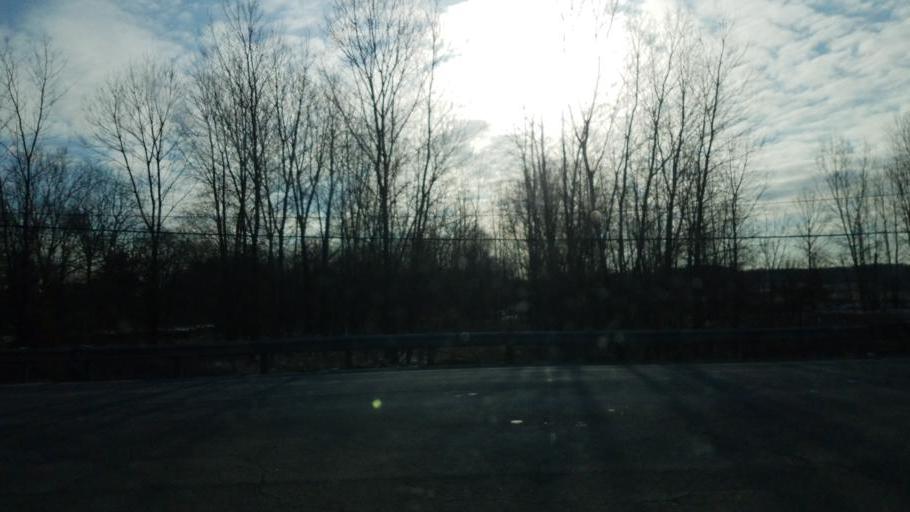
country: US
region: Ohio
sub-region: Richland County
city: Lexington
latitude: 40.6176
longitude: -82.5898
